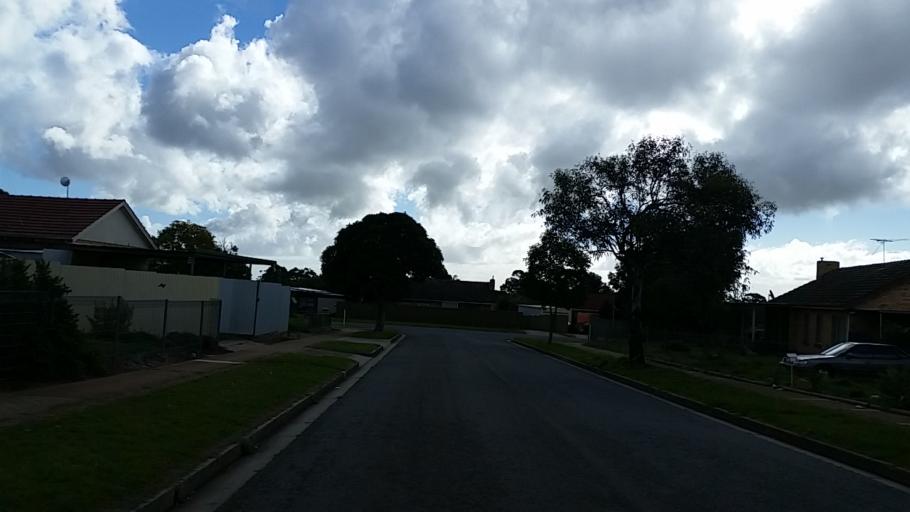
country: AU
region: South Australia
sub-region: Salisbury
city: Elizabeth
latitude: -34.7263
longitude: 138.6831
